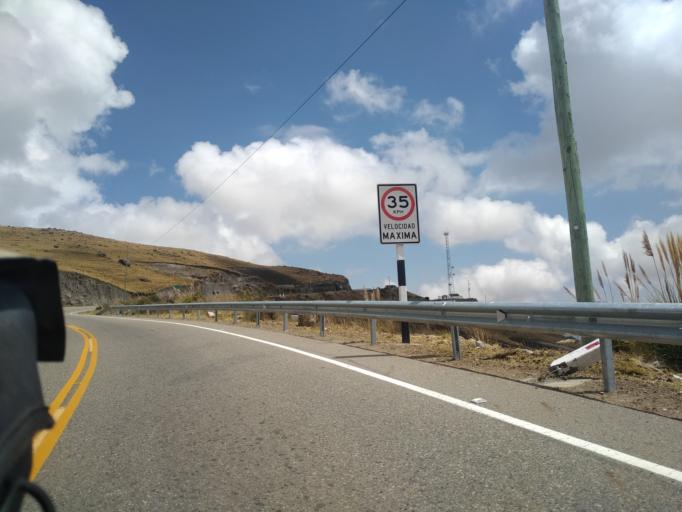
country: PE
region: La Libertad
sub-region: Provincia de Santiago de Chuco
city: Quiruvilca
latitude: -7.9193
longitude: -78.1575
